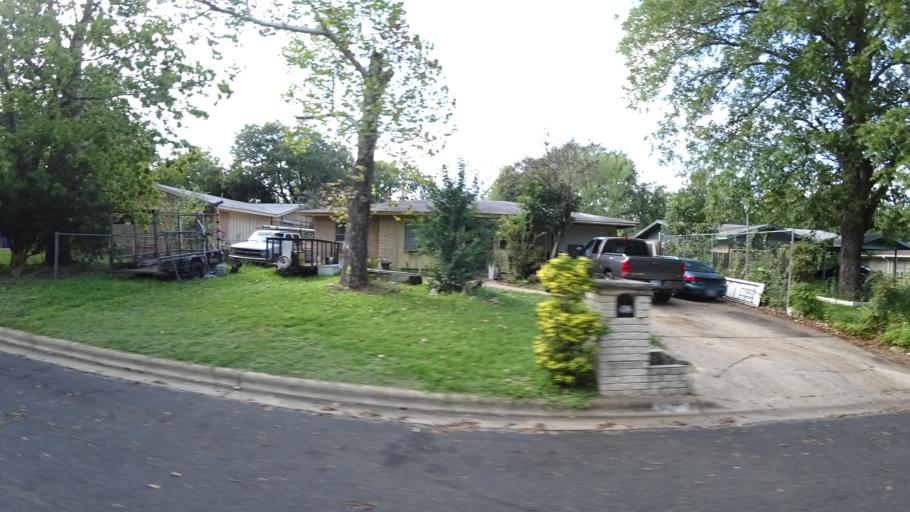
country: US
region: Texas
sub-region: Travis County
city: Rollingwood
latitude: 30.2087
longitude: -97.7910
